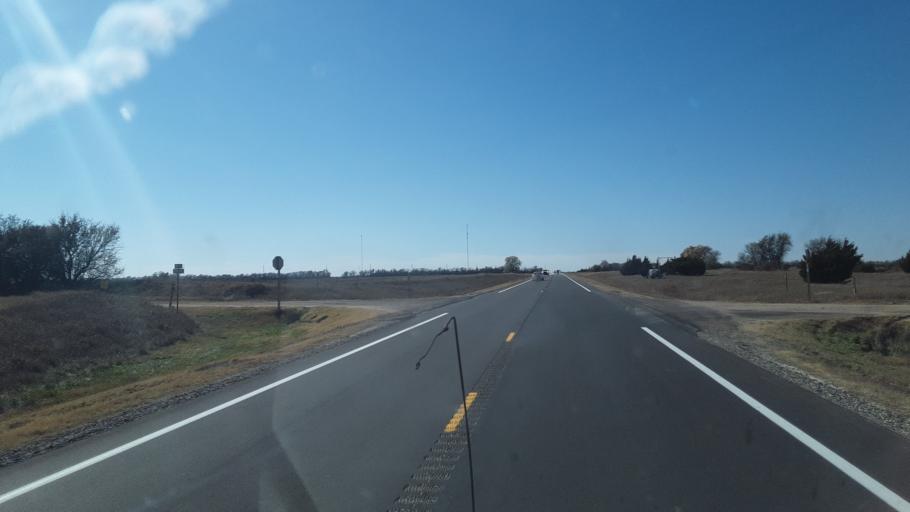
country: US
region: Kansas
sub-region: Rice County
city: Lyons
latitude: 38.3756
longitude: -98.1270
